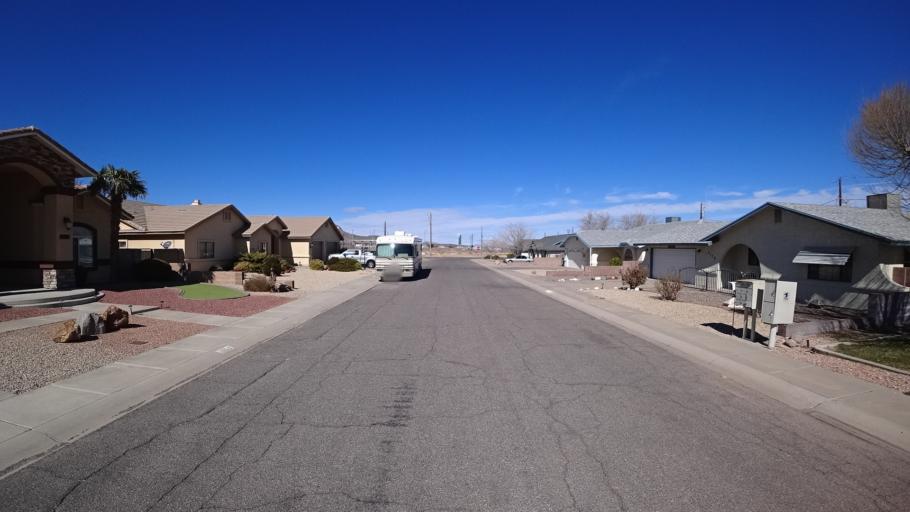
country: US
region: Arizona
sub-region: Mohave County
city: Kingman
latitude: 35.2142
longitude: -114.0435
